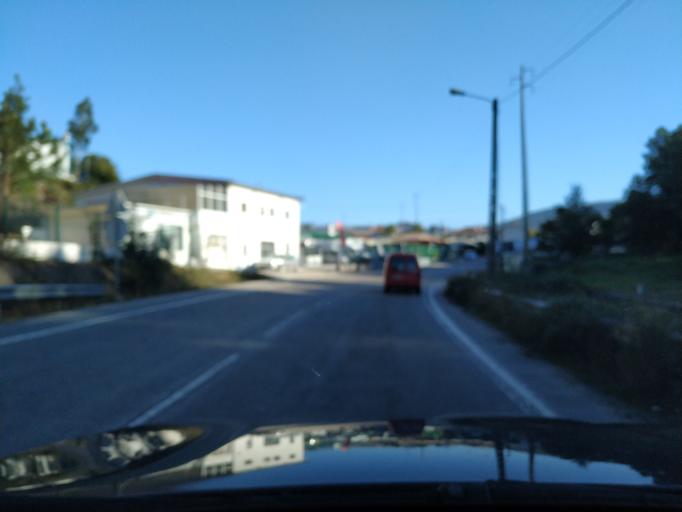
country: PT
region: Aveiro
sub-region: Oliveira de Azemeis
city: Vila Cha
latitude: 40.8791
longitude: -8.4282
